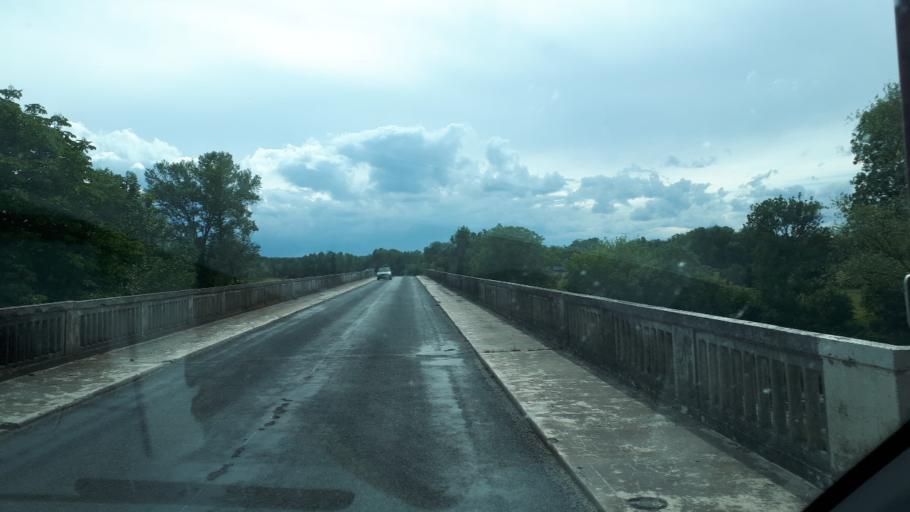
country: FR
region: Centre
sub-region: Departement du Cher
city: Mehun-sur-Yevre
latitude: 47.0805
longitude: 2.1969
